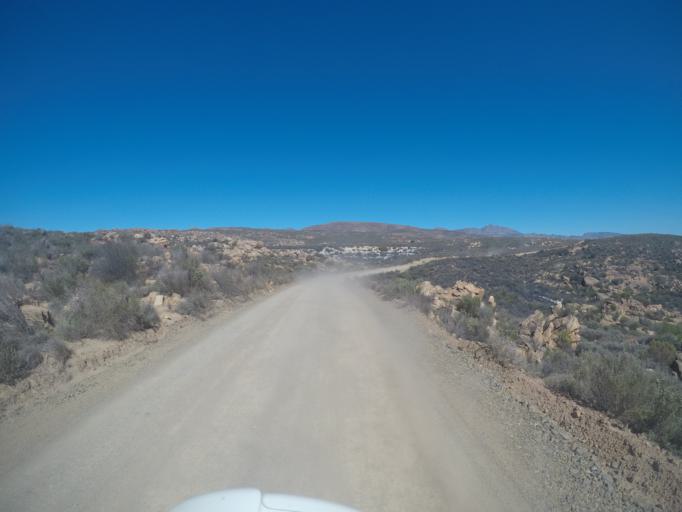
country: ZA
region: Western Cape
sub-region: West Coast District Municipality
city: Clanwilliam
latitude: -32.5065
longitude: 19.3004
